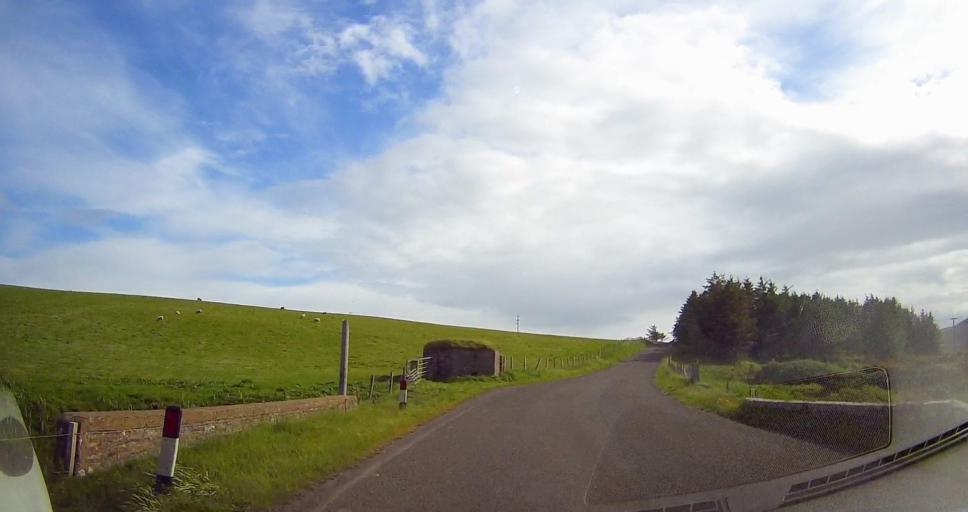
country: GB
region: Scotland
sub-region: Orkney Islands
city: Stromness
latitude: 58.8262
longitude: -3.2091
